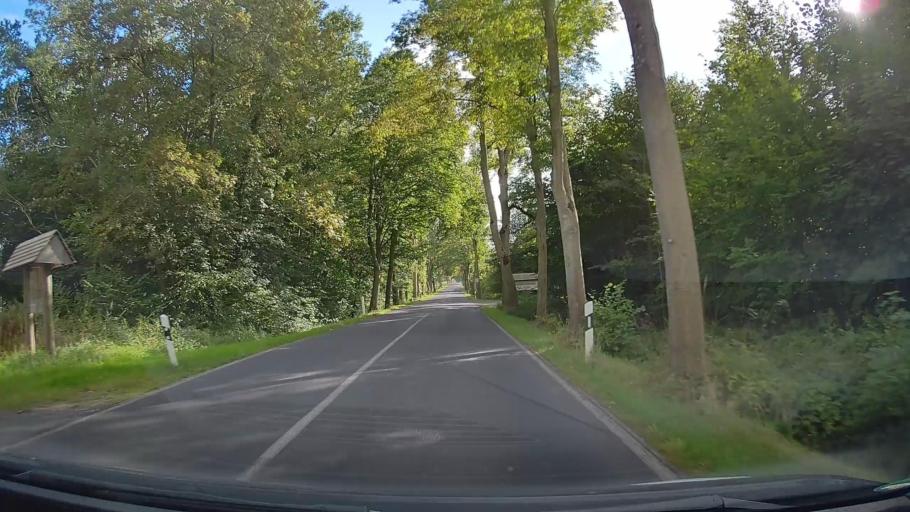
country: DE
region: Mecklenburg-Vorpommern
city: Putbus
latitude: 54.3737
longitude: 13.4803
